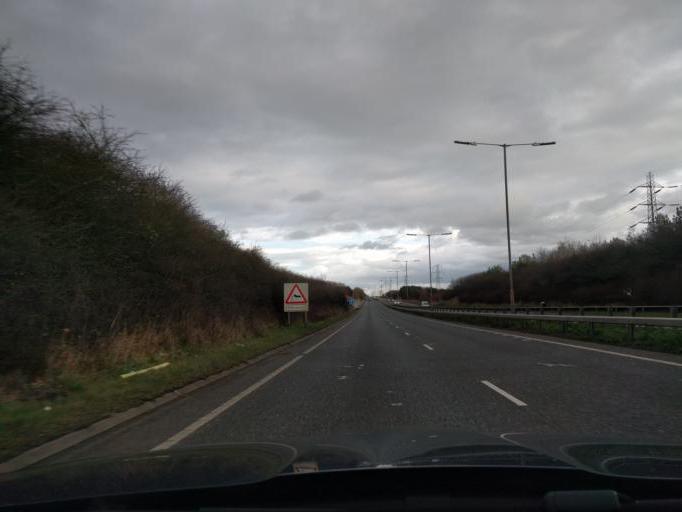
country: GB
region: England
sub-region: Northumberland
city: Newbiggin-by-the-Sea
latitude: 55.1594
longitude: -1.5406
